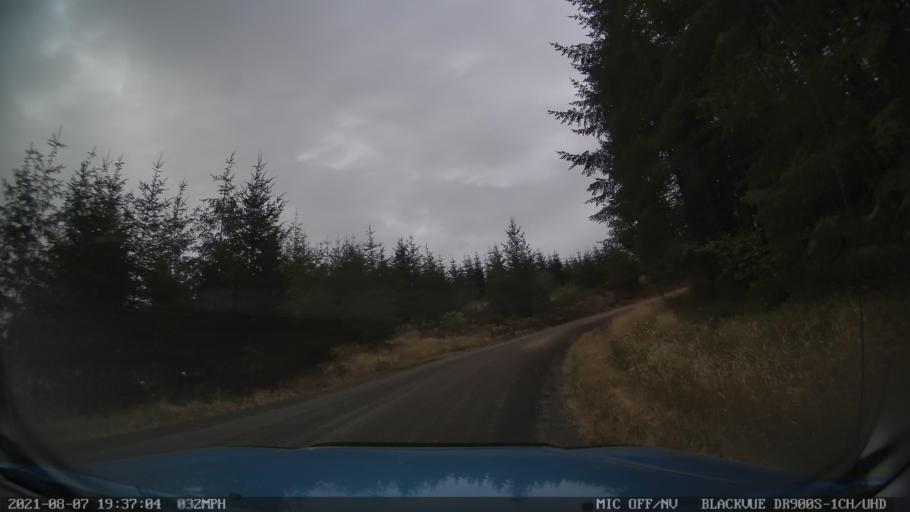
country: US
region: Oregon
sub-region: Marion County
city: Silverton
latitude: 44.9386
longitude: -122.6566
